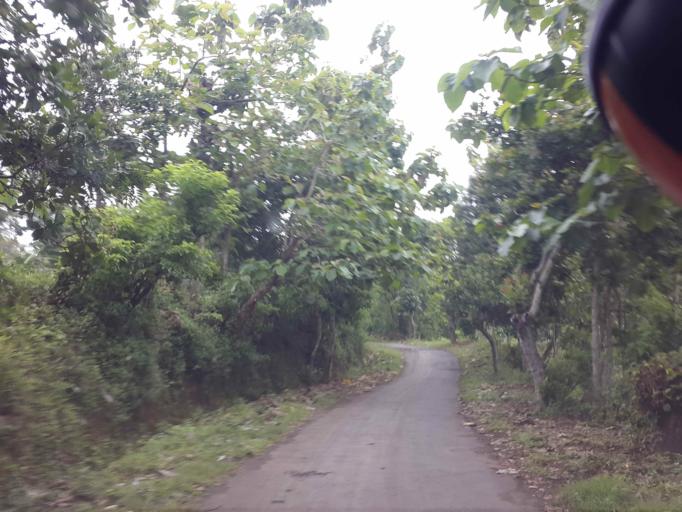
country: ID
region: East Java
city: Ponorogo
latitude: -7.7753
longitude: 111.3289
